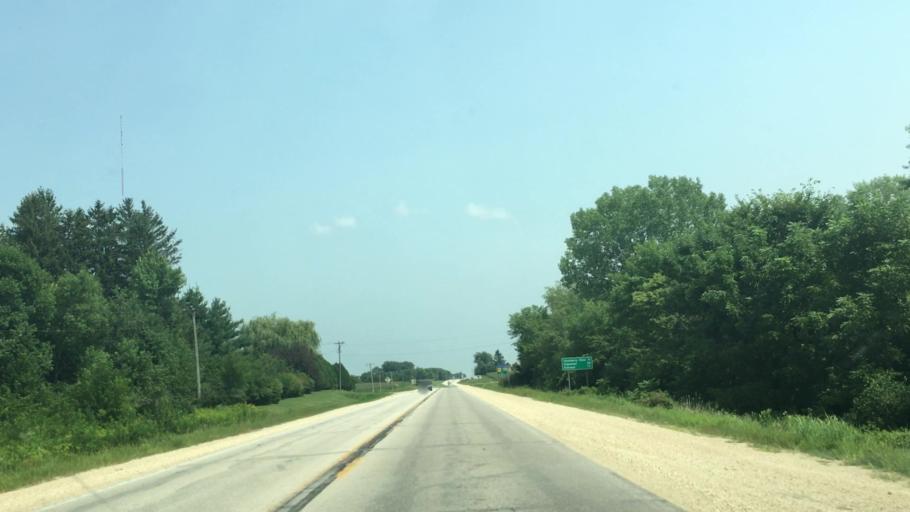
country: US
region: Iowa
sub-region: Fayette County
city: Oelwein
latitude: 42.6792
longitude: -91.8917
